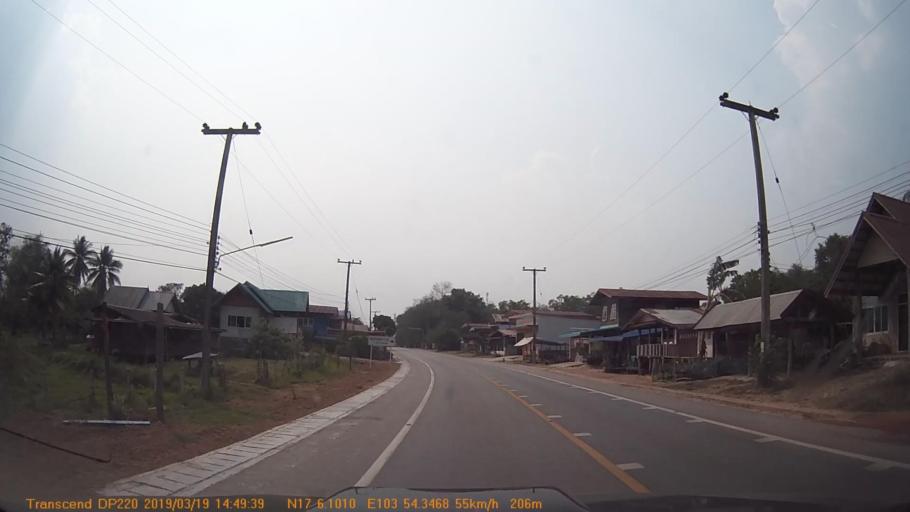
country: TH
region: Sakon Nakhon
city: Kut Bak
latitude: 17.1018
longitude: 103.9055
